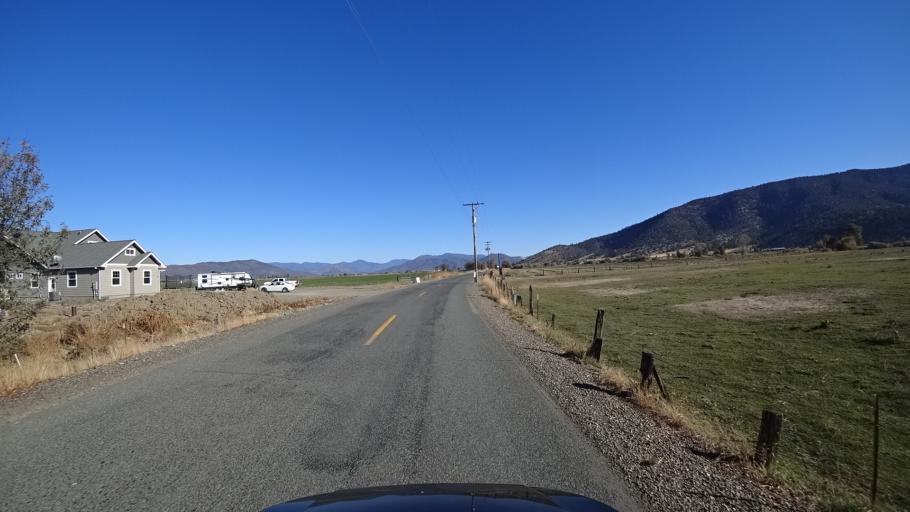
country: US
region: California
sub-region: Siskiyou County
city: Yreka
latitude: 41.5116
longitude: -122.8554
